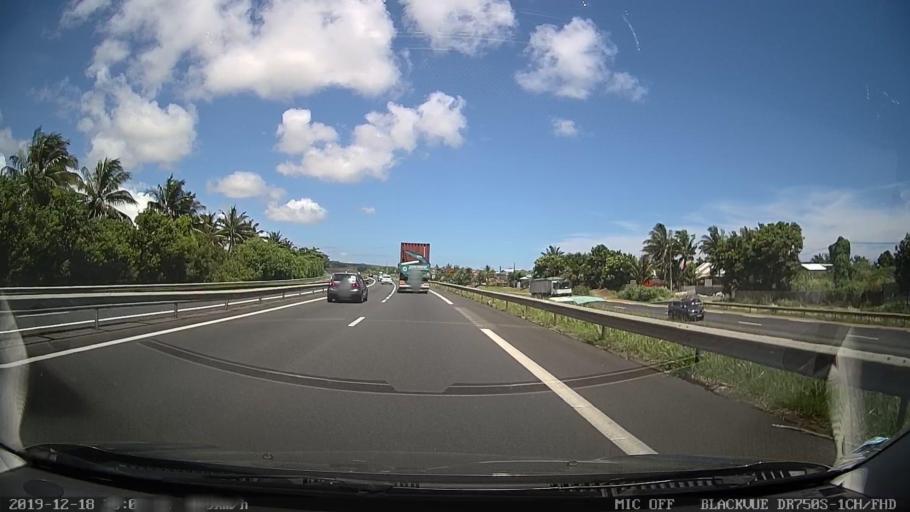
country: RE
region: Reunion
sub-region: Reunion
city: Sainte-Suzanne
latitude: -20.9164
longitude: 55.6231
